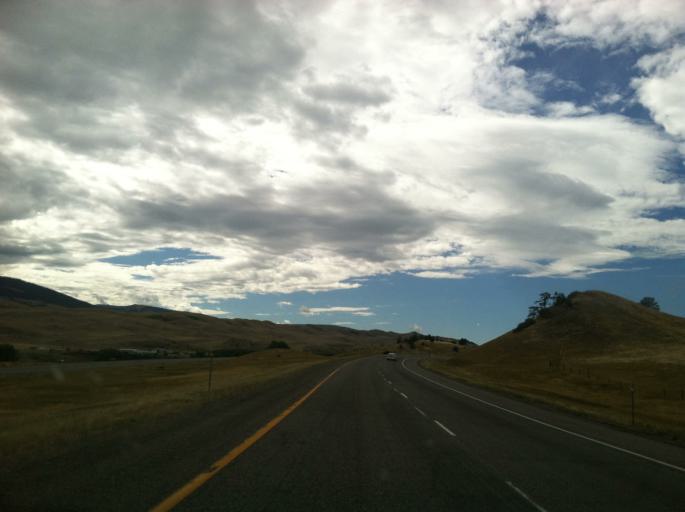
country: US
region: Montana
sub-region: Park County
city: Livingston
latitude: 45.6613
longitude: -110.6499
